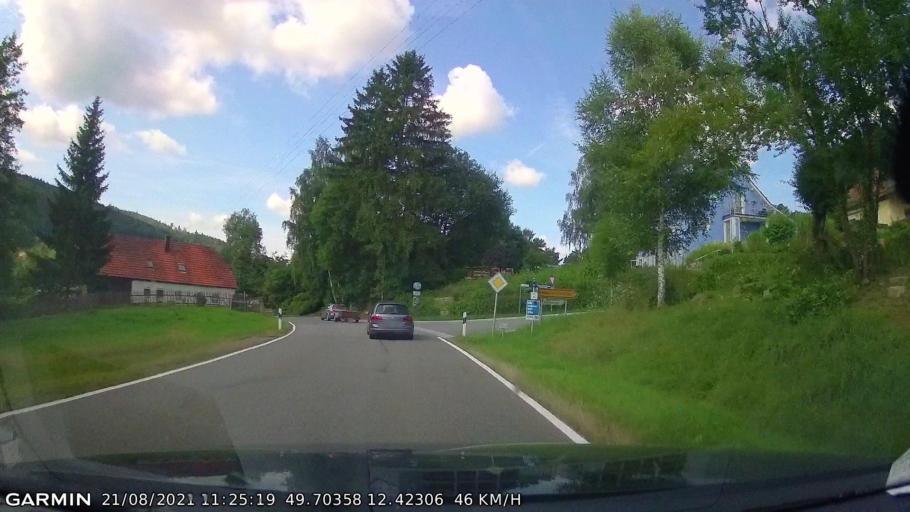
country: DE
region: Bavaria
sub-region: Upper Palatinate
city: Georgenberg
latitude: 49.7035
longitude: 12.4232
